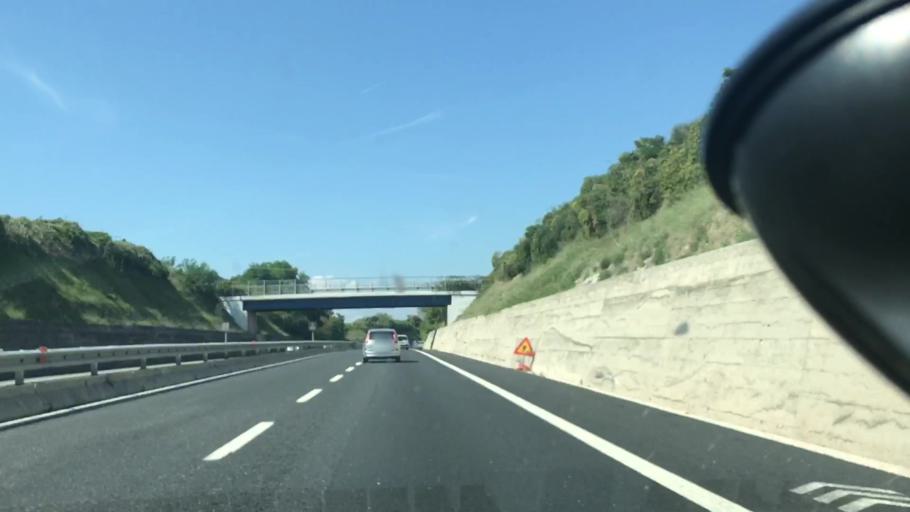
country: IT
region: Abruzzo
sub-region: Provincia di Chieti
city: Tollo
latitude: 42.3622
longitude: 14.3304
